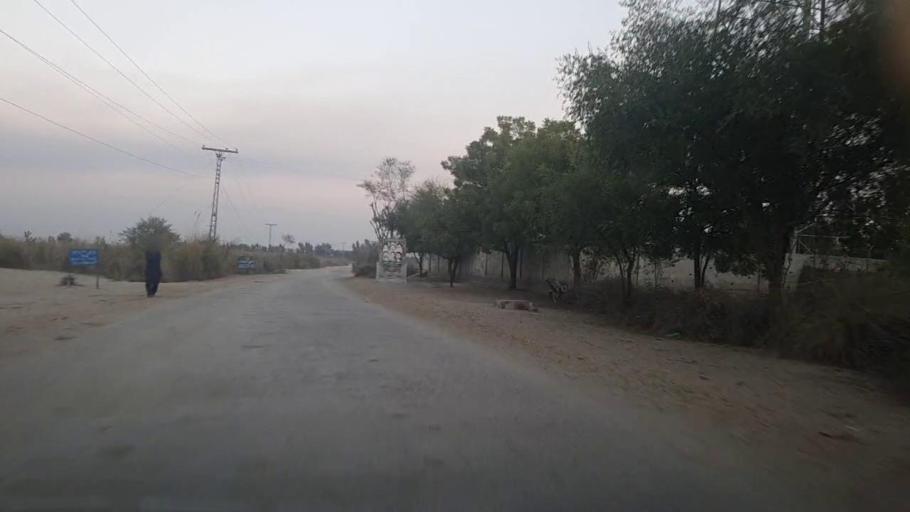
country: PK
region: Sindh
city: Kandiari
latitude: 26.6829
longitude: 68.9389
